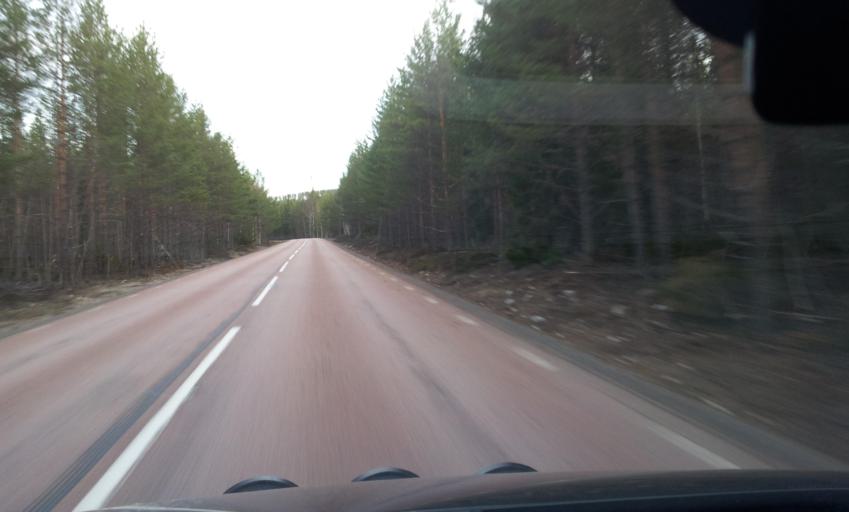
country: SE
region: Gaevleborg
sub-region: Ljusdals Kommun
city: Farila
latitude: 61.9807
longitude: 15.8575
